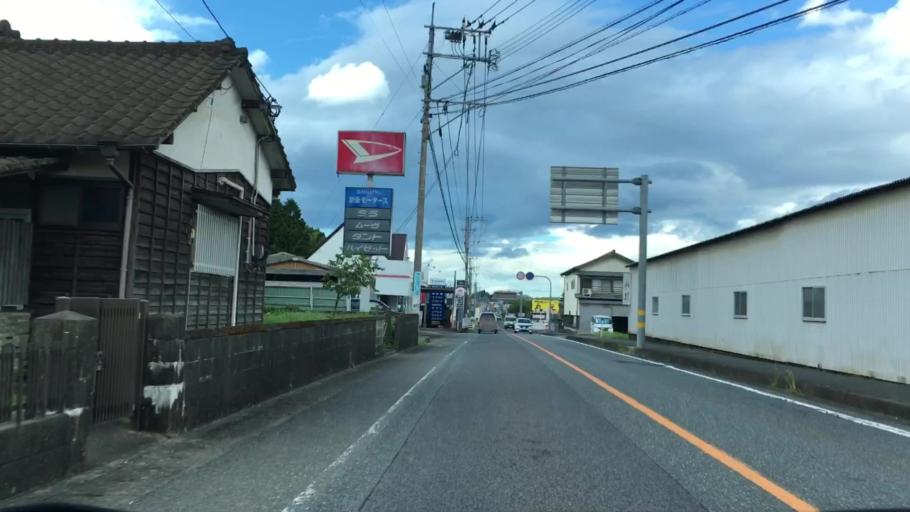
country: JP
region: Saga Prefecture
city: Imaricho-ko
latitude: 33.1978
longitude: 129.8505
